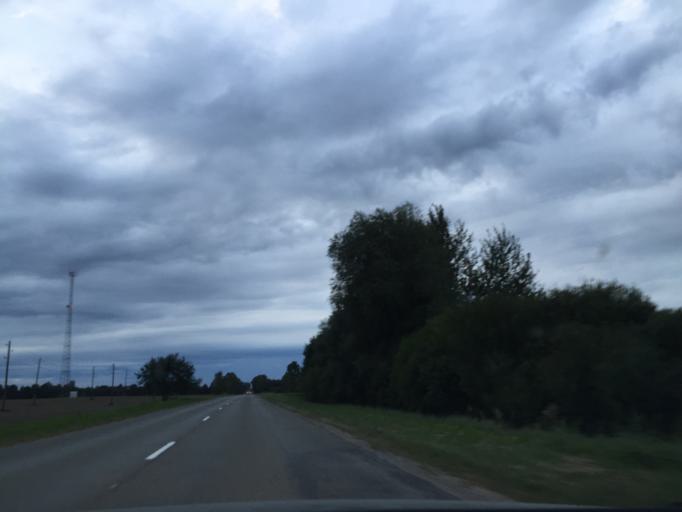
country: LV
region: Vecumnieki
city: Vecumnieki
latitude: 56.5375
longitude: 24.5477
